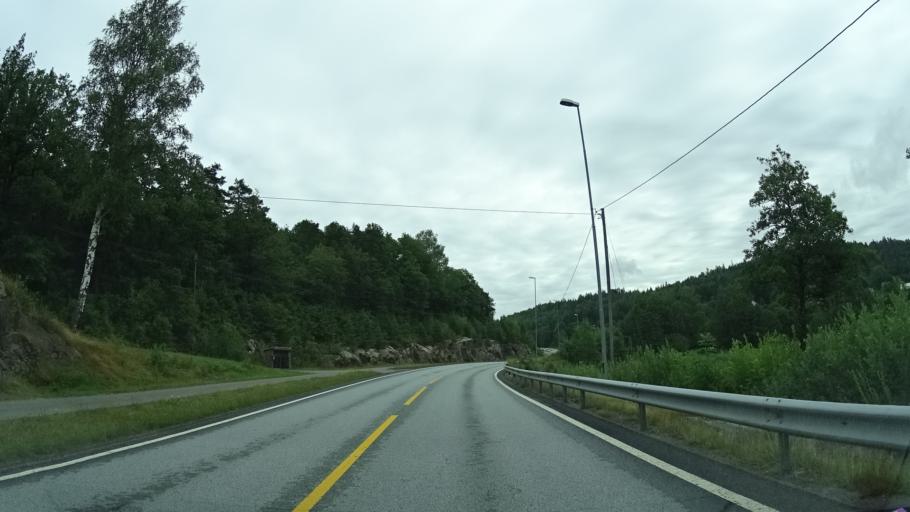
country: NO
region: Aust-Agder
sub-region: Arendal
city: Arendal
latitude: 58.5609
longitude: 8.8160
